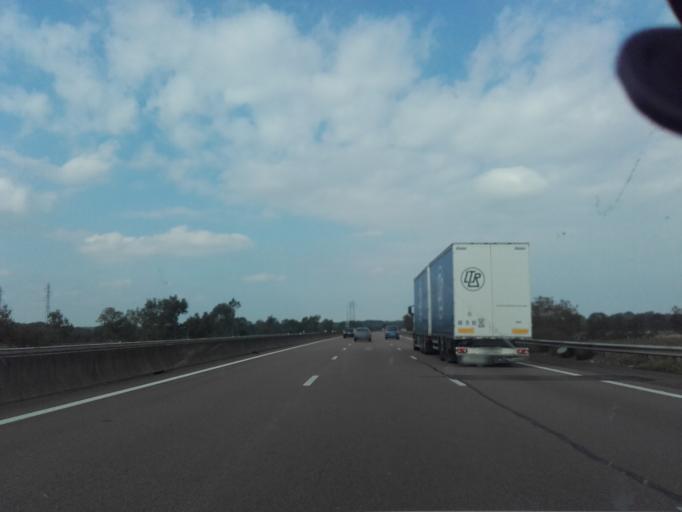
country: FR
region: Bourgogne
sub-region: Departement de Saone-et-Loire
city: Sennecey-le-Grand
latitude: 46.6701
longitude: 4.8491
